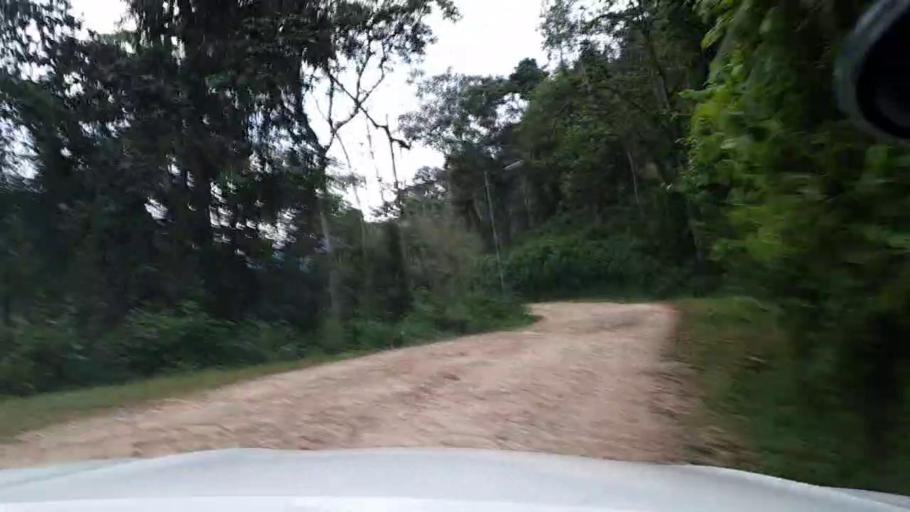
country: RW
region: Western Province
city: Cyangugu
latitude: -2.5570
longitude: 29.2317
